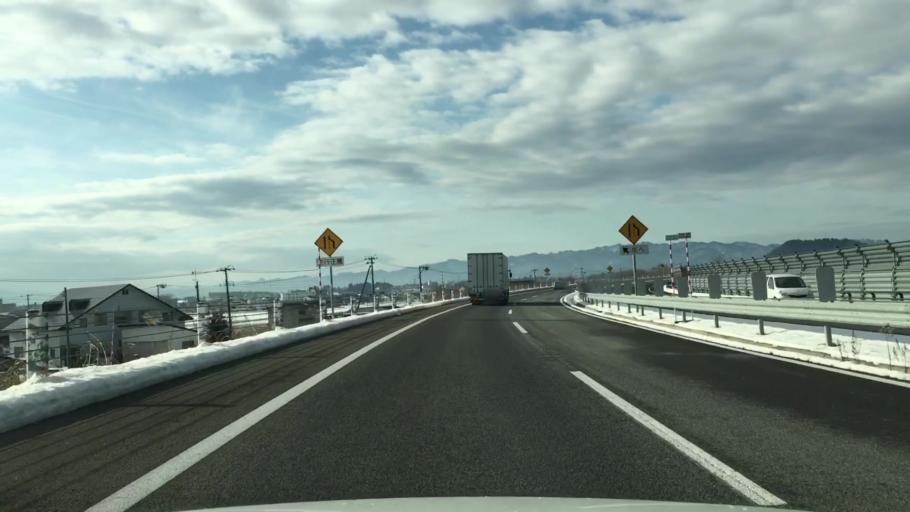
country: JP
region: Akita
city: Odate
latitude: 40.2932
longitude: 140.5523
